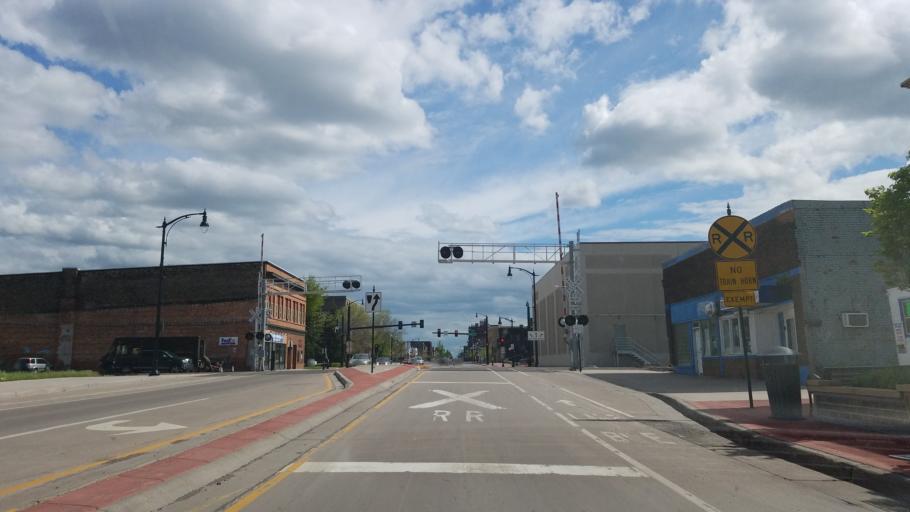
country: US
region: Wisconsin
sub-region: Douglas County
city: Superior
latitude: 46.7292
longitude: -92.1040
